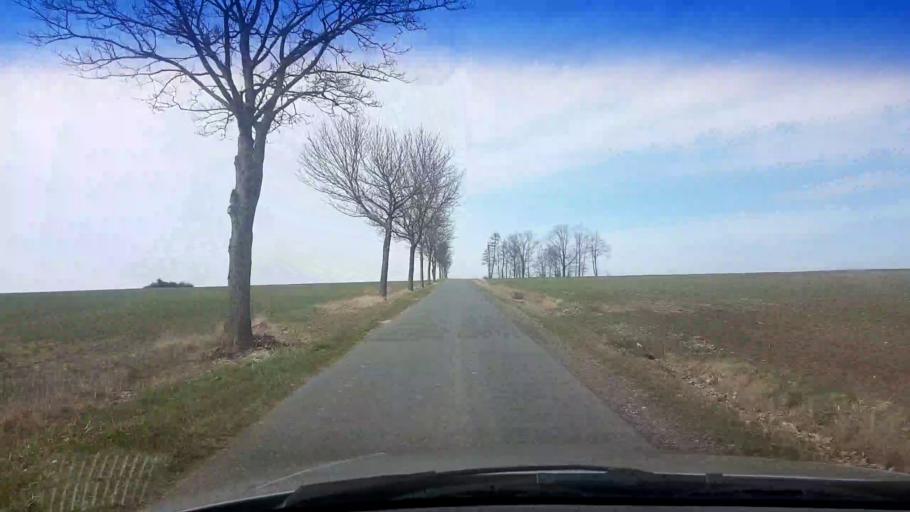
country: DE
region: Bavaria
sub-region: Upper Franconia
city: Burgebrach
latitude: 49.8065
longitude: 10.7609
